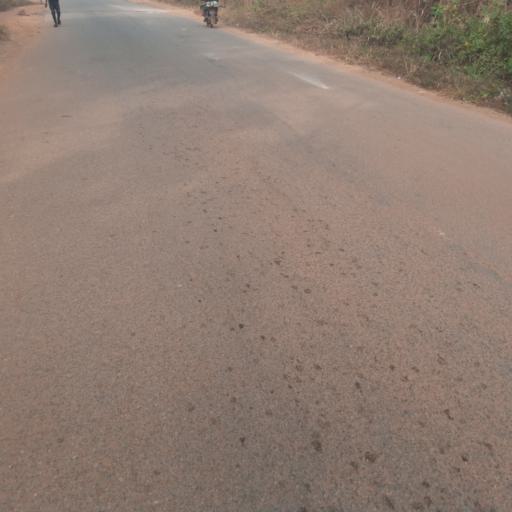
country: NG
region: Ondo
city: Ilare
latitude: 7.2992
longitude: 5.1389
